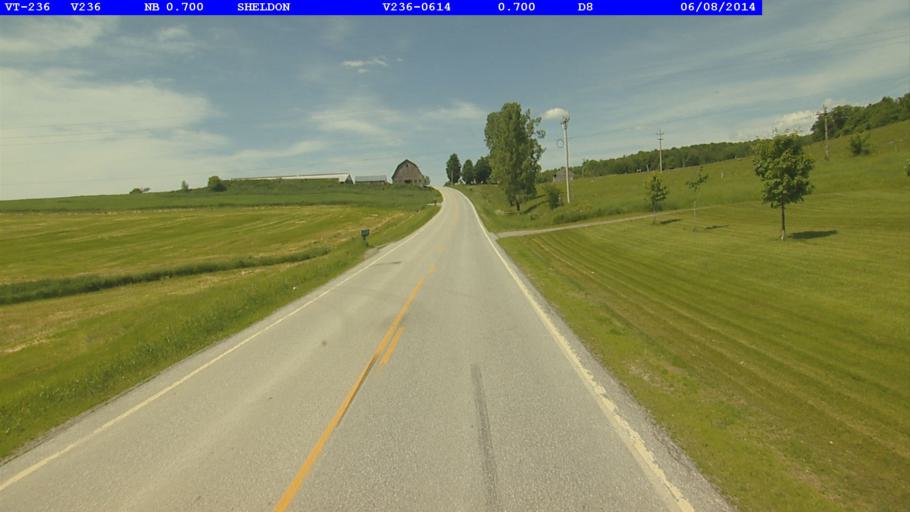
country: US
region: Vermont
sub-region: Franklin County
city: Enosburg Falls
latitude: 44.9210
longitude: -72.8652
